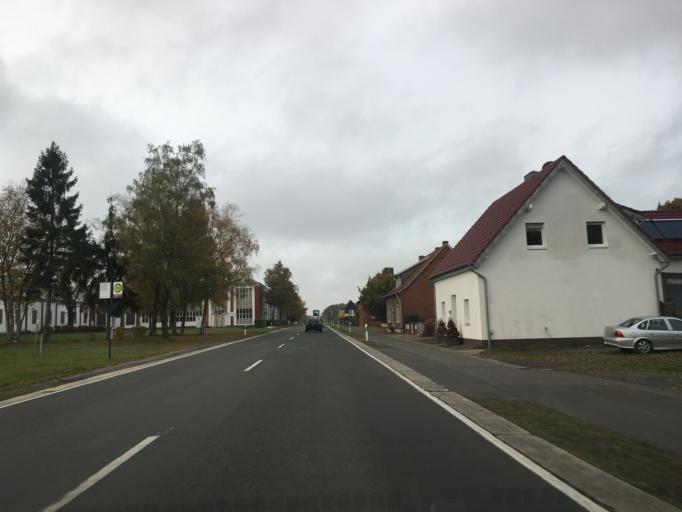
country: DE
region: North Rhine-Westphalia
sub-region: Regierungsbezirk Munster
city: Altenberge
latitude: 52.0954
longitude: 7.4154
